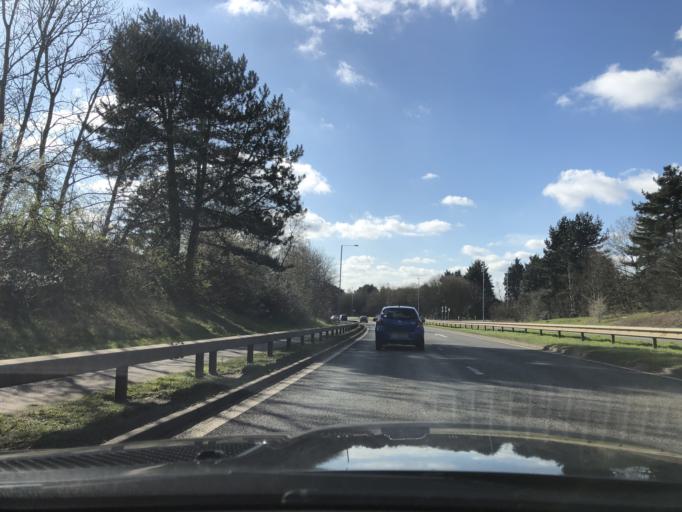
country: GB
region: England
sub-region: Northamptonshire
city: Northampton
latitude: 52.2491
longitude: -0.8368
